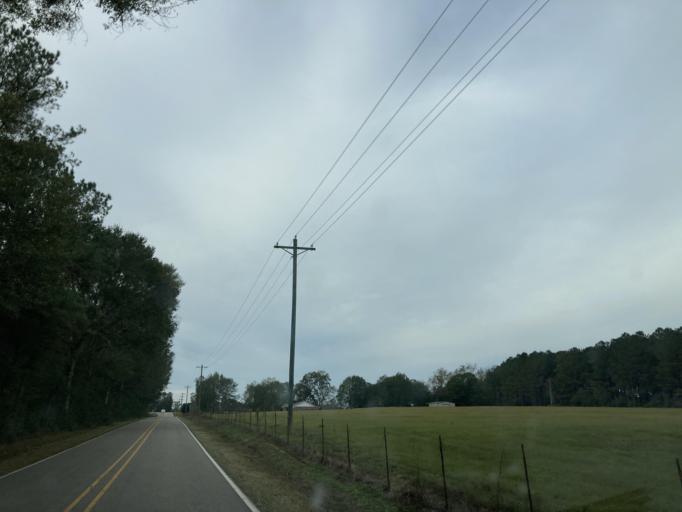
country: US
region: Mississippi
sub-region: Lamar County
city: Purvis
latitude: 31.1126
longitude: -89.4698
